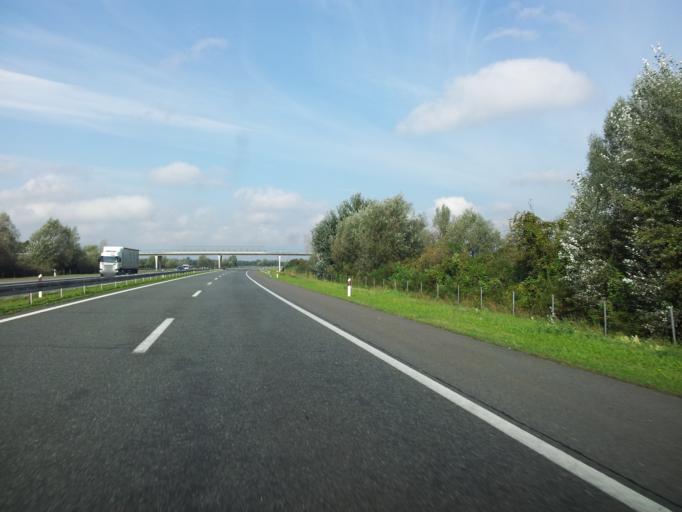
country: HR
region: Brodsko-Posavska
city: Garcin
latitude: 45.1556
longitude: 18.1926
